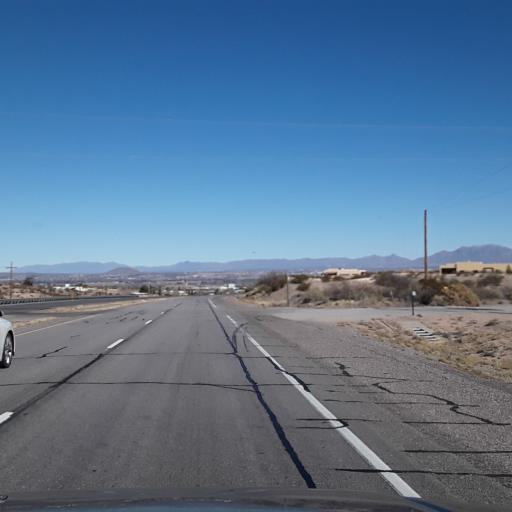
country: US
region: New Mexico
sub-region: Dona Ana County
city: Mesilla
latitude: 32.2871
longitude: -106.8750
